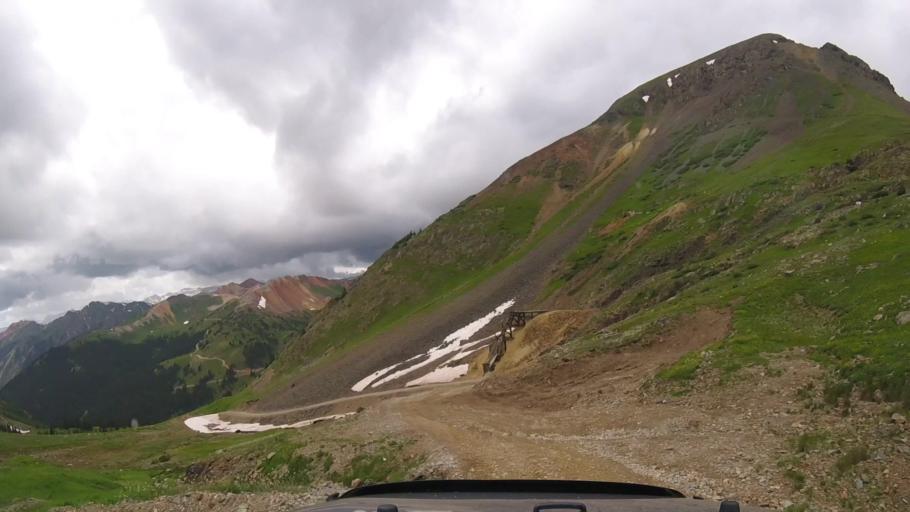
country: US
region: Colorado
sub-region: San Juan County
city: Silverton
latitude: 37.9136
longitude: -107.6296
